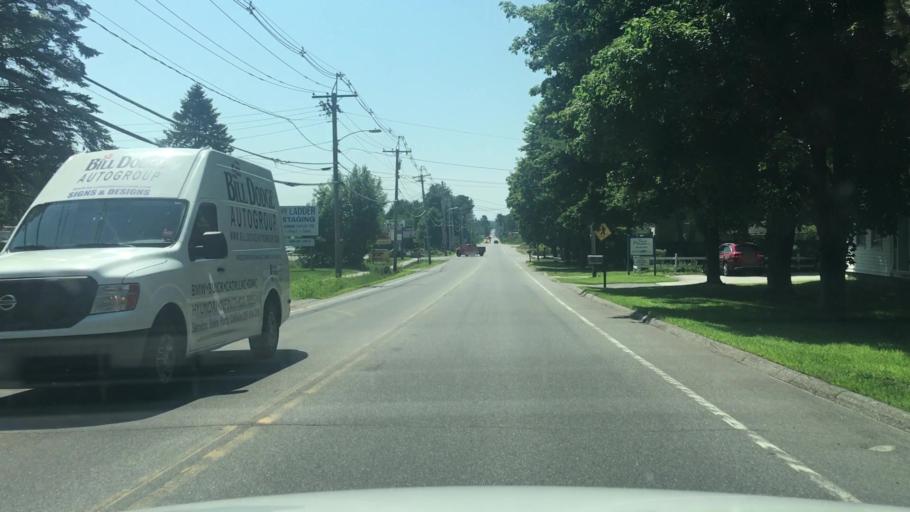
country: US
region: Maine
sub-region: Cumberland County
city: New Gloucester
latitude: 43.8831
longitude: -70.3300
